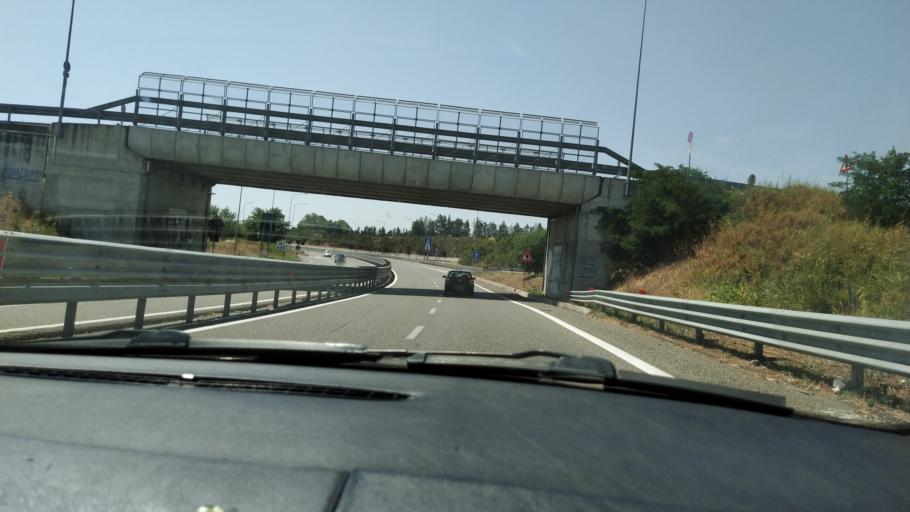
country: IT
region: Basilicate
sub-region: Provincia di Matera
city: Marconia
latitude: 40.3654
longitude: 16.7799
